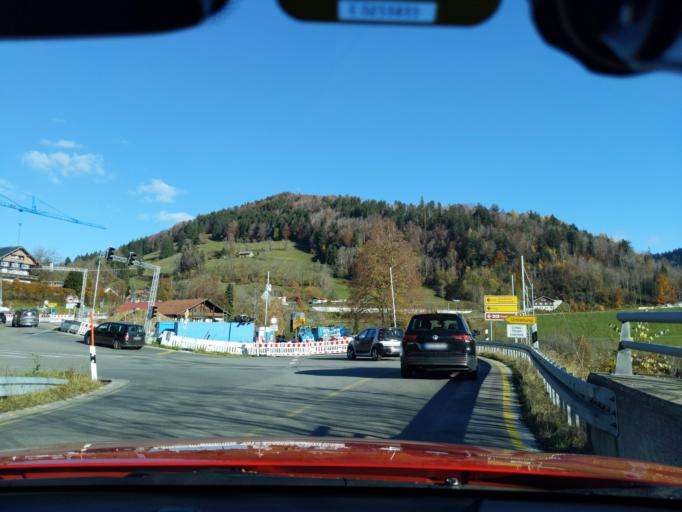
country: DE
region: Bavaria
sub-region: Swabia
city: Oberstaufen
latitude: 47.5515
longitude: 10.0216
